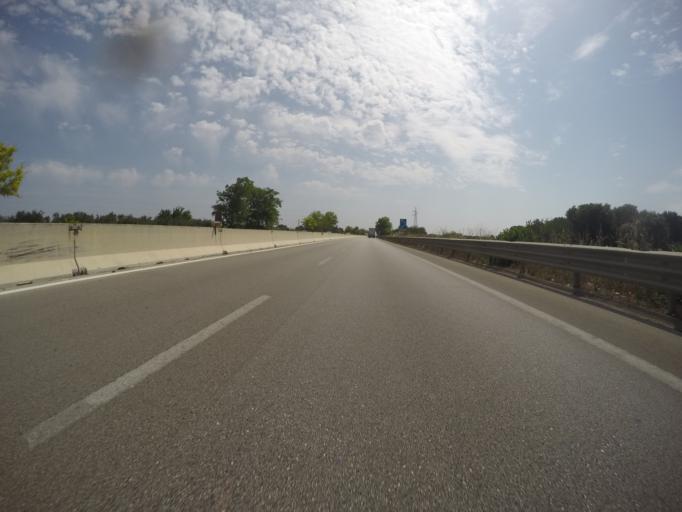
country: IT
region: Apulia
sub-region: Provincia di Brindisi
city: Oria
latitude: 40.5332
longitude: 17.6271
